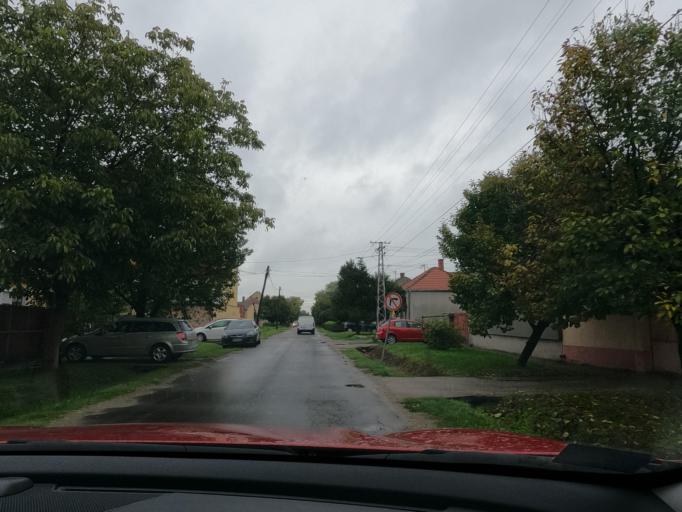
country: RS
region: Autonomna Pokrajina Vojvodina
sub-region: Sremski Okrug
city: Stara Pazova
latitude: 44.9851
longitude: 20.1405
